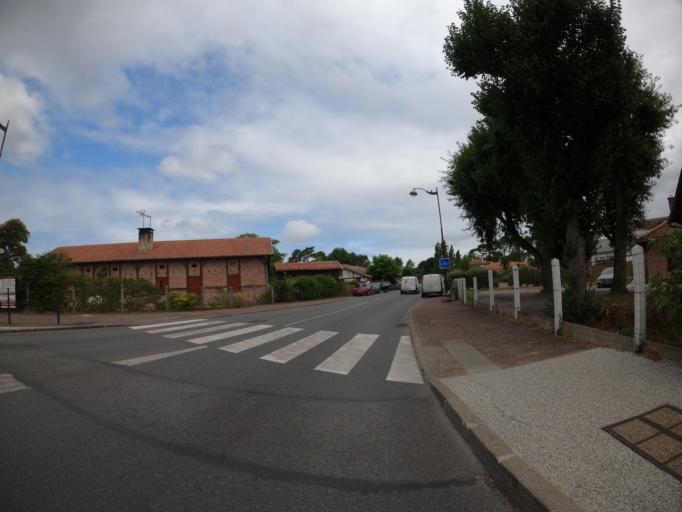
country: FR
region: Aquitaine
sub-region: Departement des Landes
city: Leon
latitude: 43.8776
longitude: -1.3028
